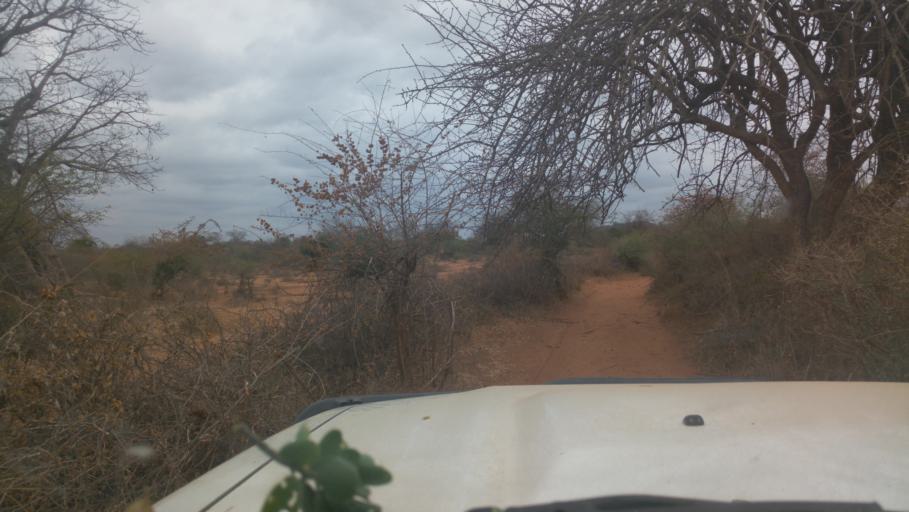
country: KE
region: Makueni
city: Makueni
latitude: -1.9727
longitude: 38.0758
